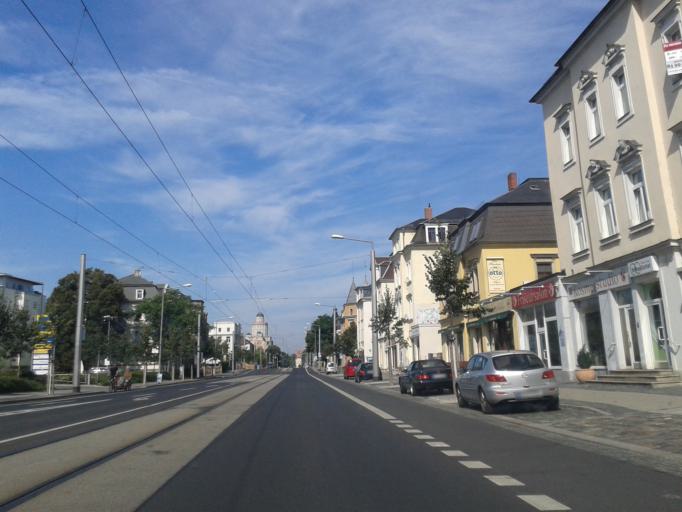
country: DE
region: Saxony
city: Albertstadt
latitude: 51.0399
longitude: 13.8050
